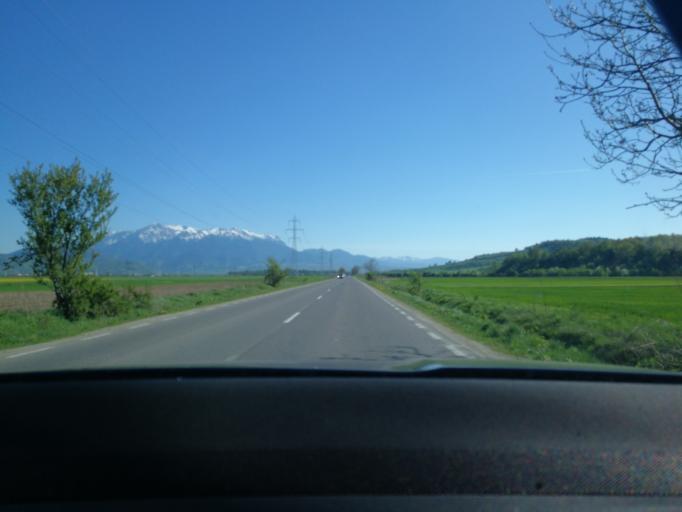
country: RO
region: Brasov
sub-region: Comuna Vulcan
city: Vulcan
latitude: 45.6205
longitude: 25.4252
